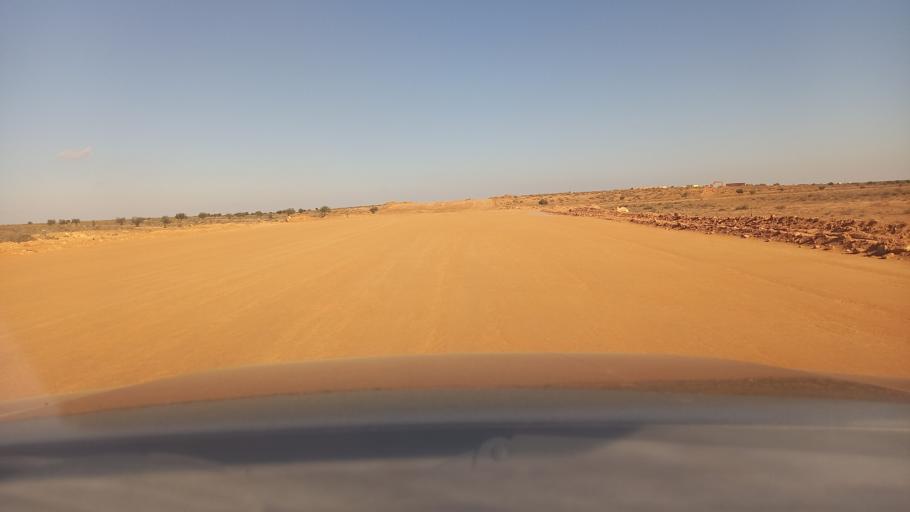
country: TN
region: Madanin
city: Medenine
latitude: 33.1713
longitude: 10.5265
